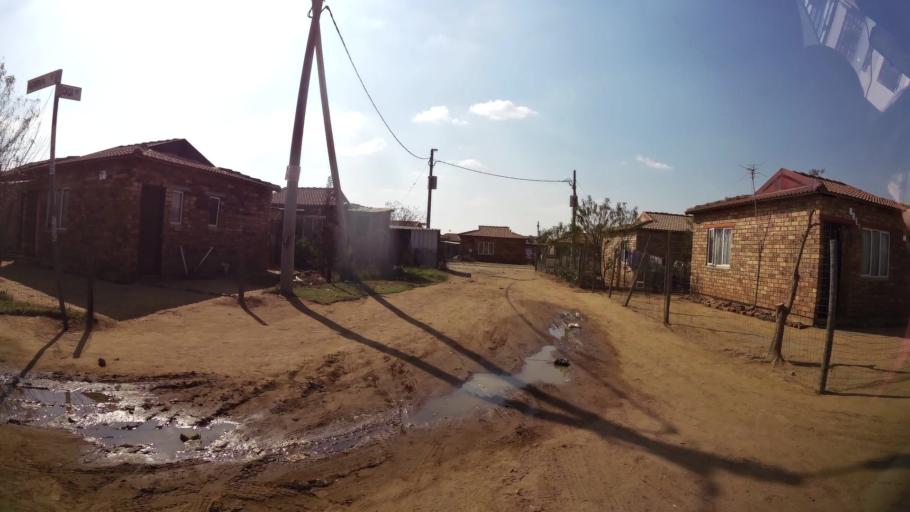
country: ZA
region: Gauteng
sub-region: Ekurhuleni Metropolitan Municipality
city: Benoni
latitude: -26.1379
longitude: 28.4097
